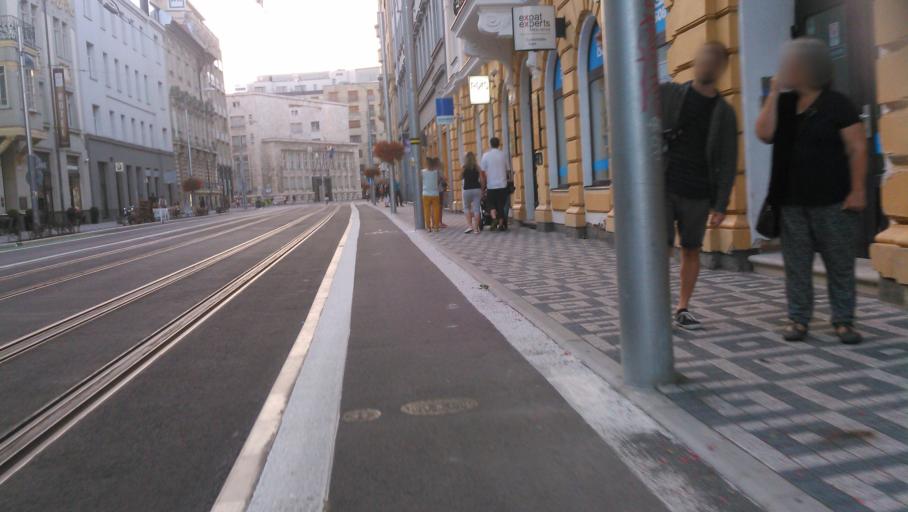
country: SK
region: Bratislavsky
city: Bratislava
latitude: 48.1425
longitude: 17.1146
